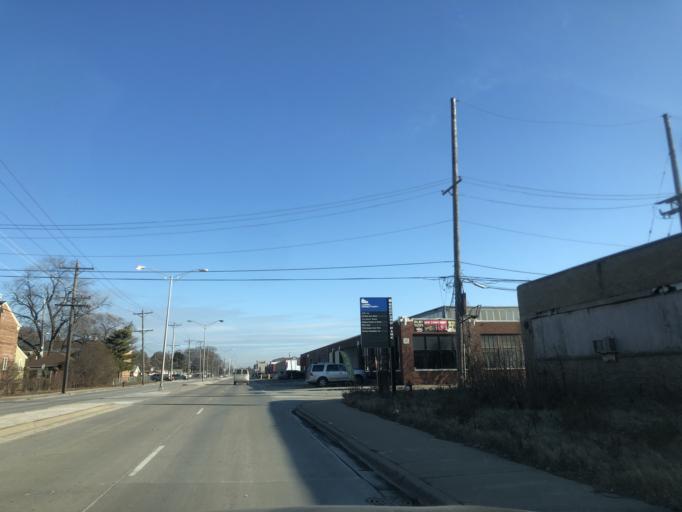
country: US
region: Illinois
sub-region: Cook County
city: Burbank
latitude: 41.7745
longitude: -87.7561
